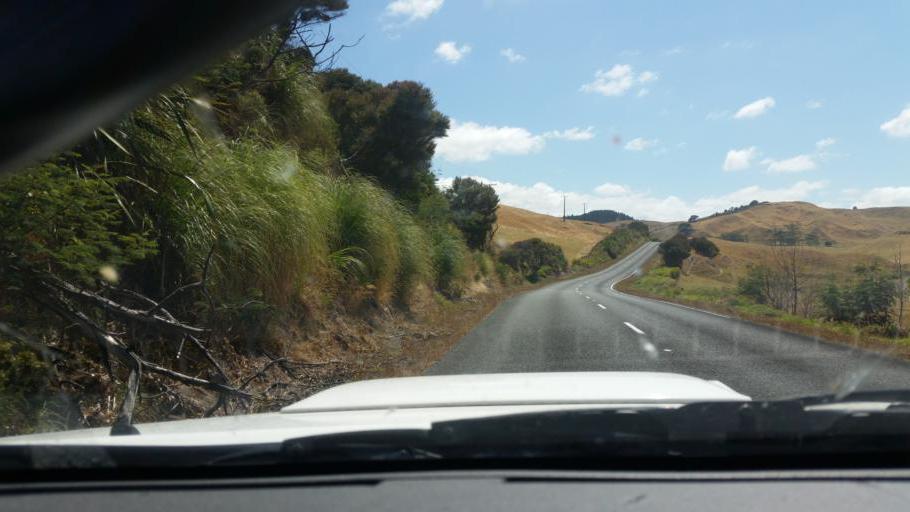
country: NZ
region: Northland
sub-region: Kaipara District
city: Dargaville
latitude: -35.8282
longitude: 173.6706
